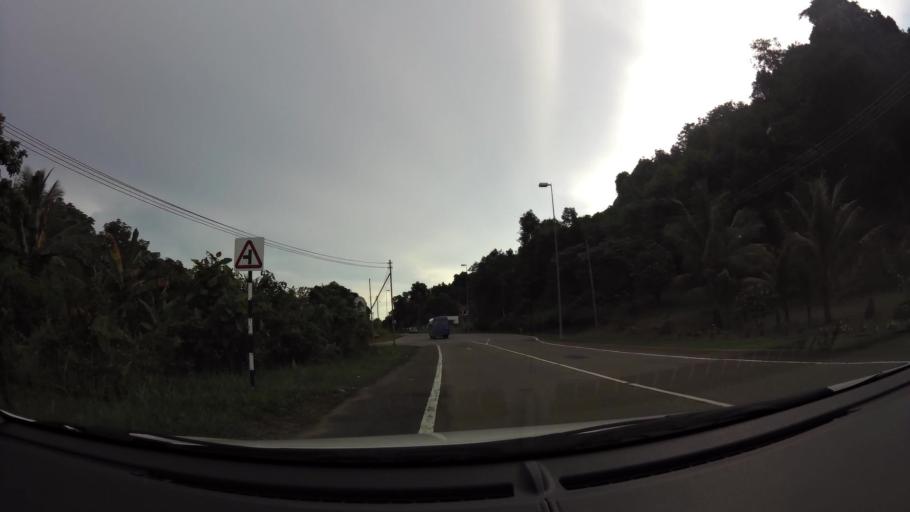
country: BN
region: Brunei and Muara
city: Bandar Seri Begawan
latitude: 4.9133
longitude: 115.0024
